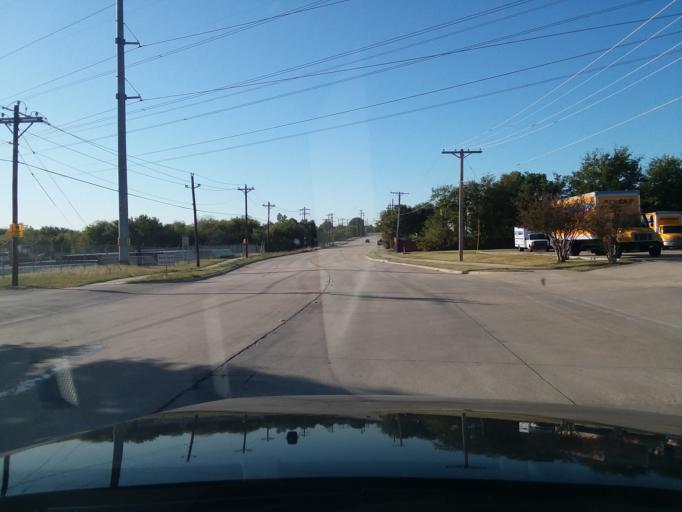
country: US
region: Texas
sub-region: Denton County
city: Highland Village
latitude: 33.0690
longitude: -97.0273
